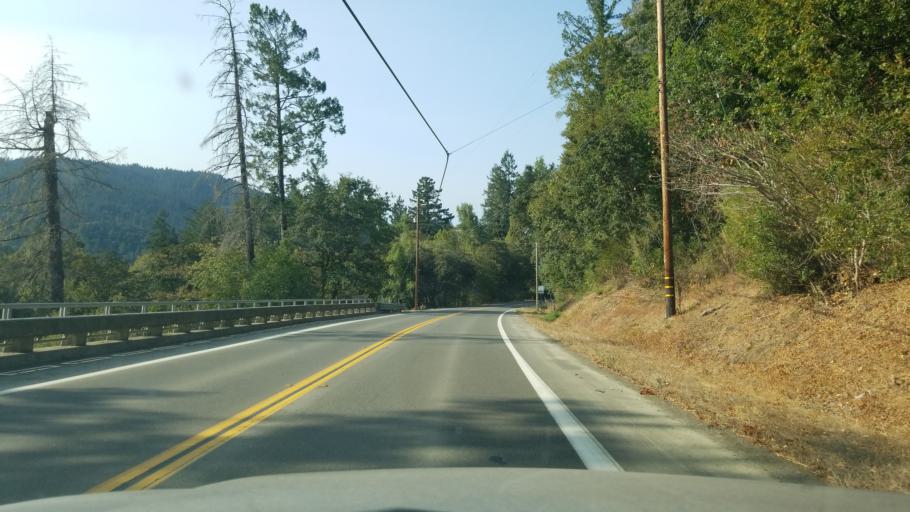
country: US
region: California
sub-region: Humboldt County
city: Redway
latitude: 40.2286
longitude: -123.8237
